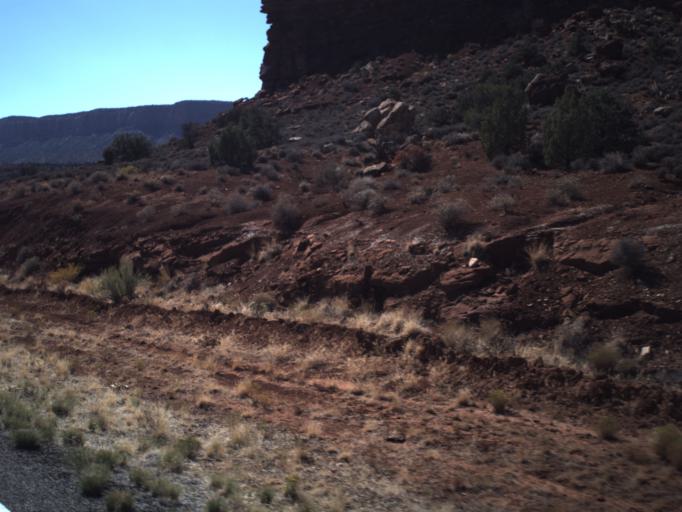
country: US
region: Utah
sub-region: San Juan County
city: Blanding
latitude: 37.7118
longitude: -110.2430
